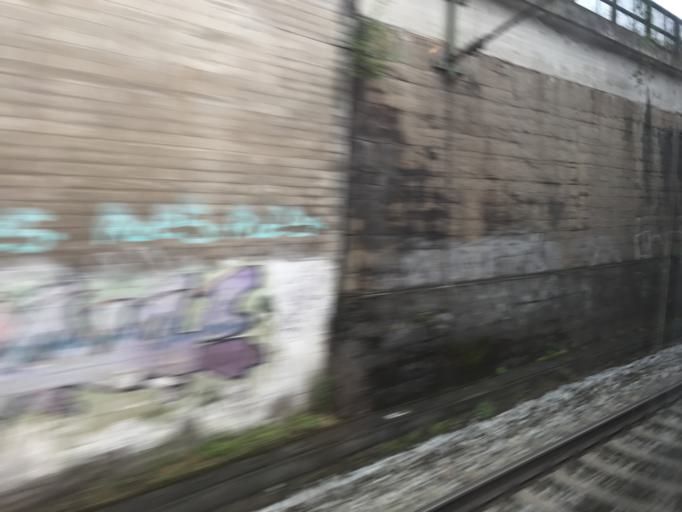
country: DE
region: Bavaria
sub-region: Upper Bavaria
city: Pasing
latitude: 48.1457
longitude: 11.4904
